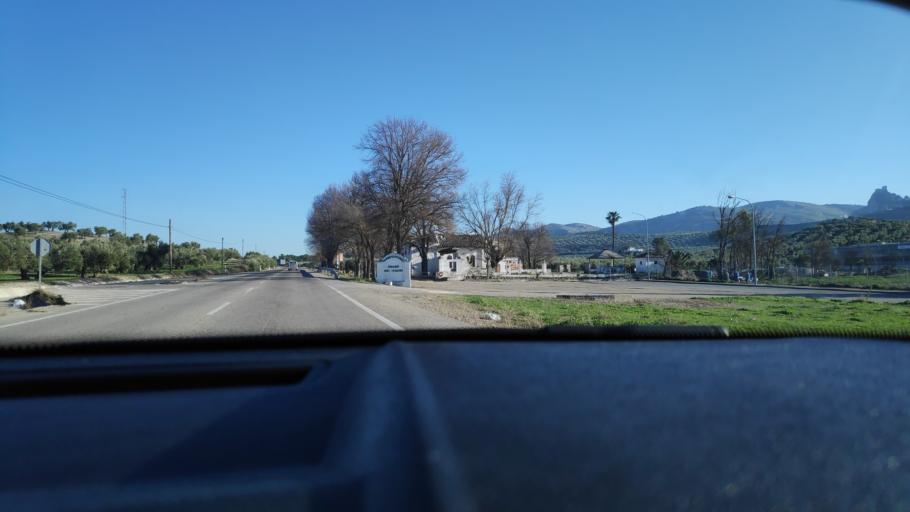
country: ES
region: Andalusia
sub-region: Province of Cordoba
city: Luque
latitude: 37.5802
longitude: -4.2814
